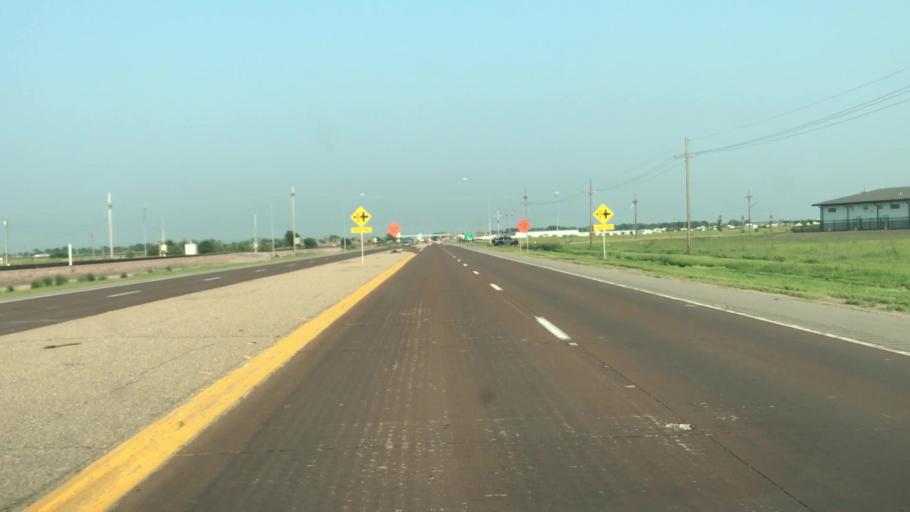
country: US
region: Nebraska
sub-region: Hall County
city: Grand Island
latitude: 40.9569
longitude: -98.3998
